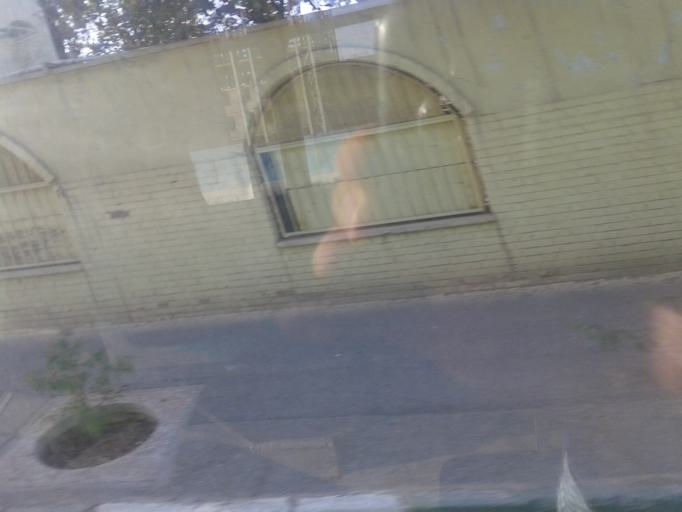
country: IR
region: Tehran
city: Tehran
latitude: 35.6317
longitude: 51.3628
